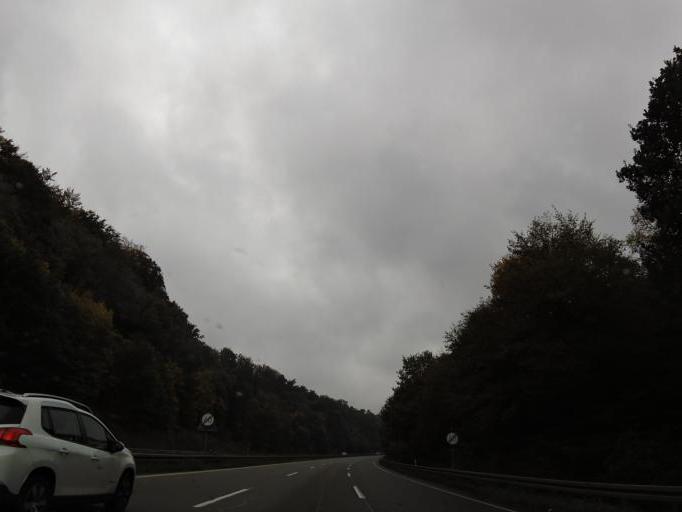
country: DE
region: Saarland
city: Sankt Ingbert
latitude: 49.2440
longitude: 7.0885
